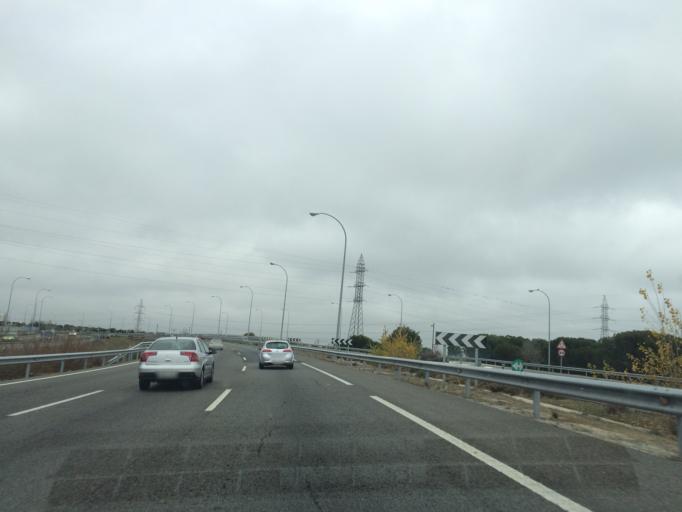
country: ES
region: Madrid
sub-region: Provincia de Madrid
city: Pozuelo de Alarcon
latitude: 40.4092
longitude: -3.8232
